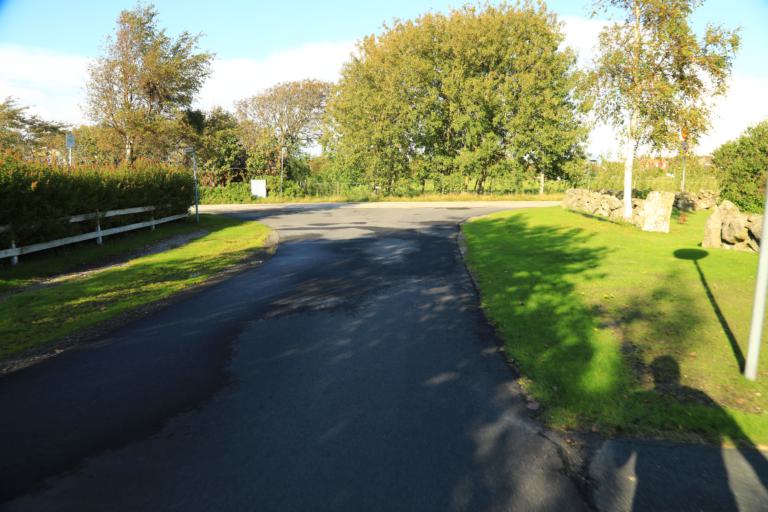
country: SE
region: Halland
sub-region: Varbergs Kommun
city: Varberg
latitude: 57.1195
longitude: 12.2058
